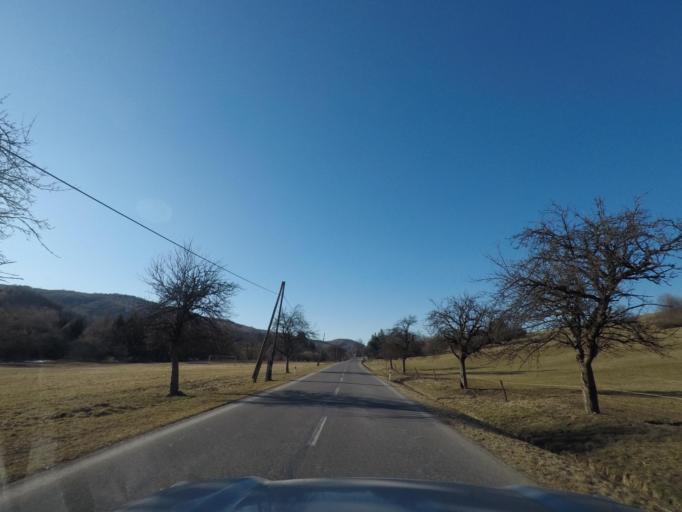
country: SK
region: Presovsky
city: Medzilaborce
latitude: 49.1878
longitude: 22.0107
